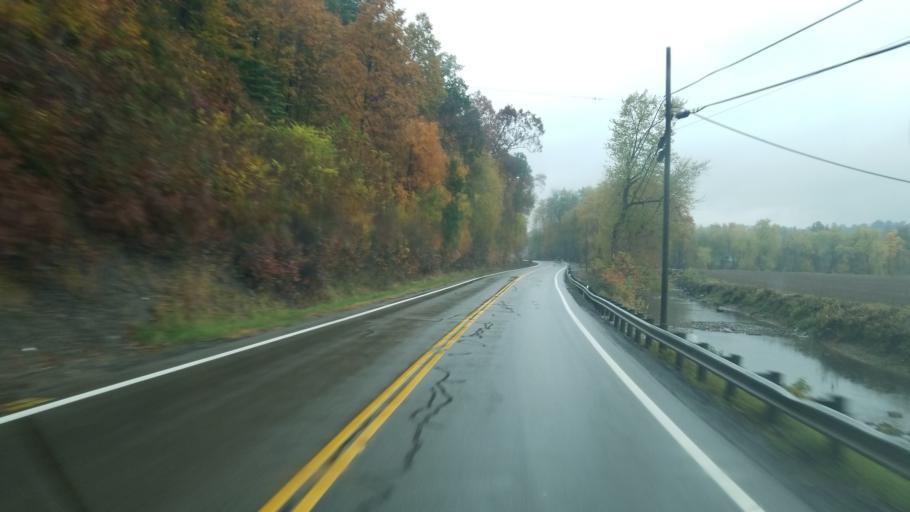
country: US
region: Ohio
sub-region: Coshocton County
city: Coshocton
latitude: 40.2966
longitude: -81.8718
